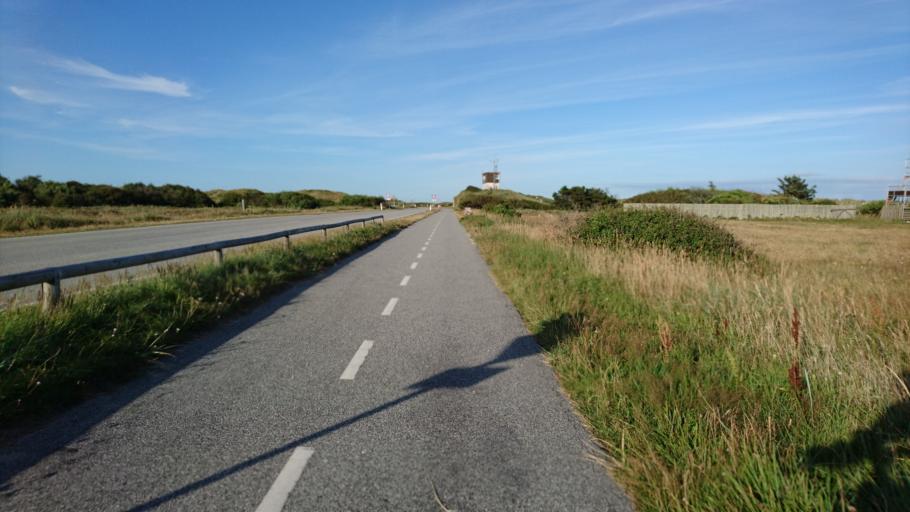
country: DK
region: North Denmark
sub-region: Frederikshavn Kommune
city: Skagen
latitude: 57.7359
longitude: 10.6292
